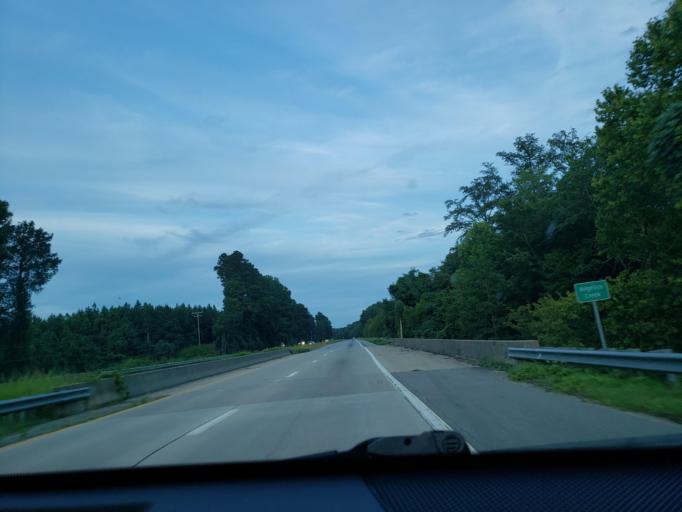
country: US
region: Virginia
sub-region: Southampton County
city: Courtland
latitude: 36.7022
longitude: -77.2512
